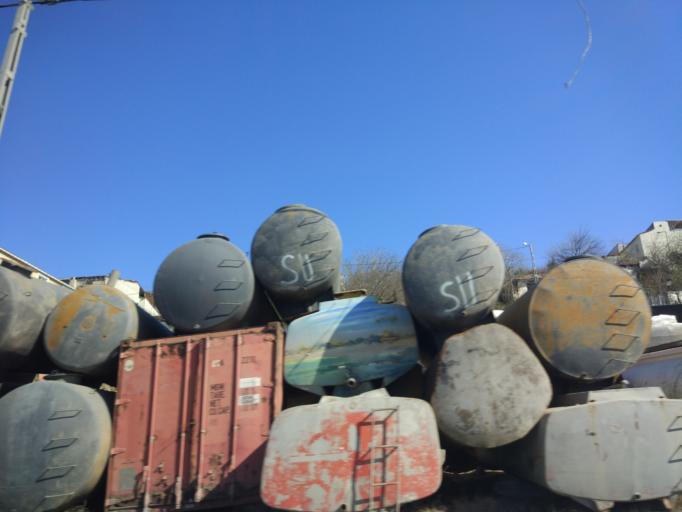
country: TR
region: Istanbul
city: Basaksehir
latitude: 41.0511
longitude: 28.7494
